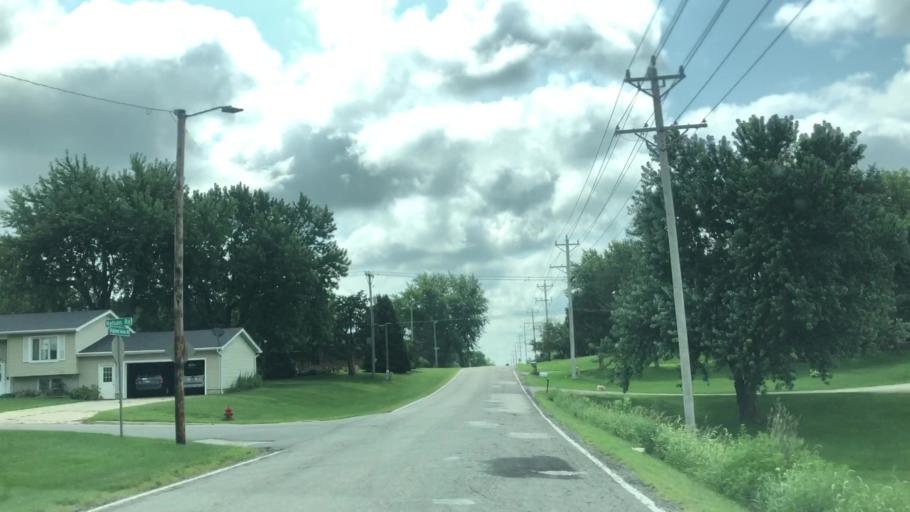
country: US
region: Iowa
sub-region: Marshall County
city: Marshalltown
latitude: 42.0424
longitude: -92.9611
